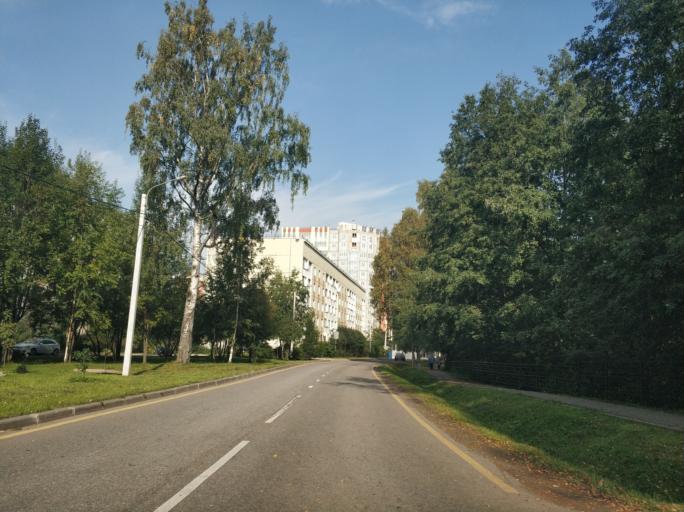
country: RU
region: Leningrad
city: Murino
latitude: 60.0393
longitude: 30.4650
